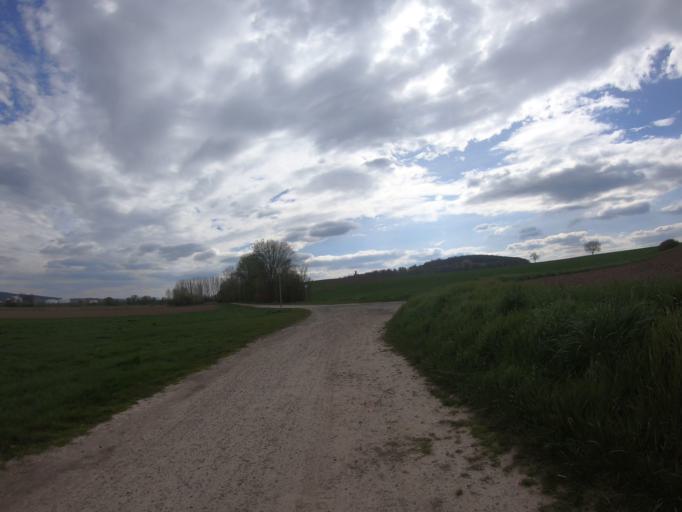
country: DE
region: Lower Saxony
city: Nordstemmen
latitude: 52.1852
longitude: 9.7773
